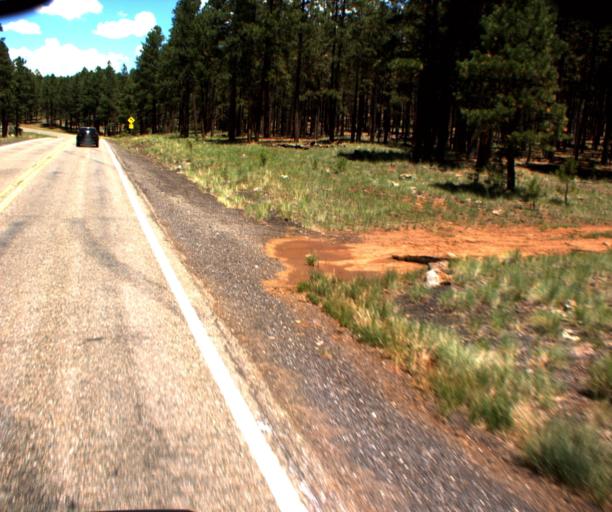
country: US
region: Arizona
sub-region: Coconino County
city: Flagstaff
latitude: 35.2972
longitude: -111.7657
